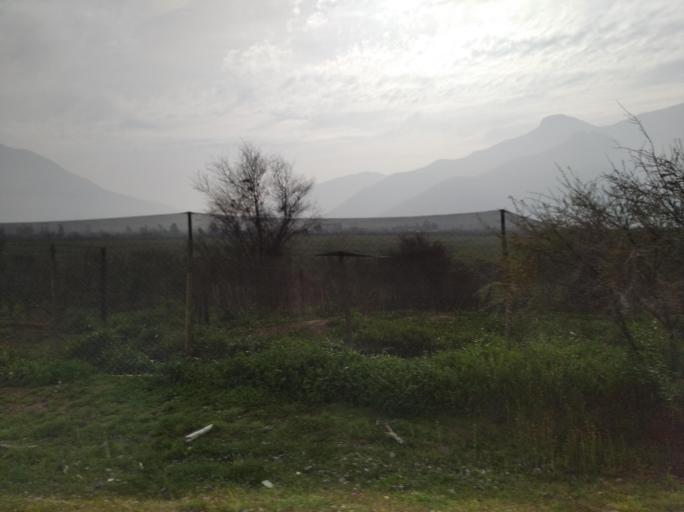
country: CL
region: Santiago Metropolitan
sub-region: Provincia de Chacabuco
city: Lampa
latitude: -33.2432
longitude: -70.9208
